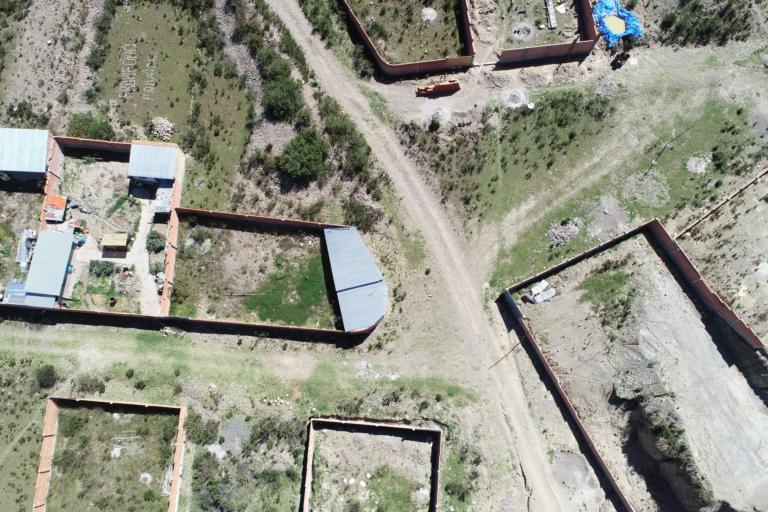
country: BO
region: La Paz
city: La Paz
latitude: -16.5031
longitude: -68.0576
